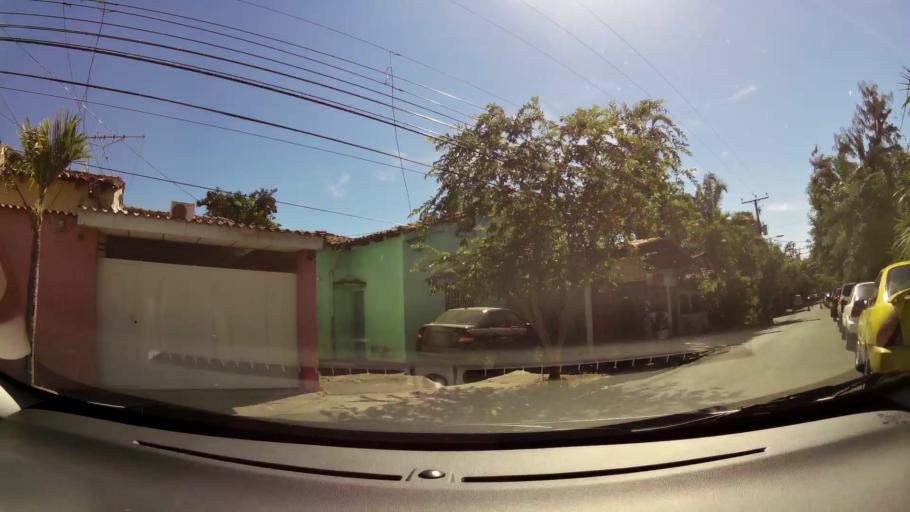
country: SV
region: San Miguel
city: San Miguel
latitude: 13.4771
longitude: -88.1705
